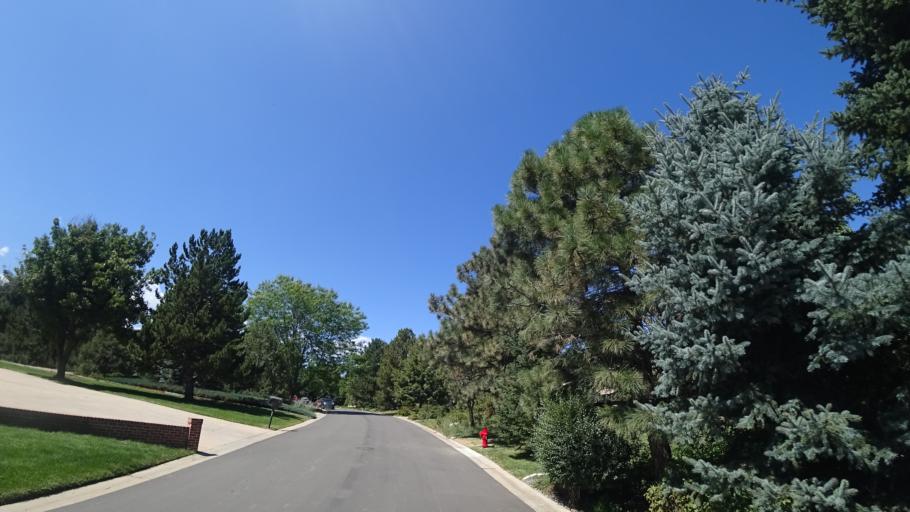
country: US
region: Colorado
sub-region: Arapahoe County
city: Greenwood Village
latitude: 39.6107
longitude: -104.9571
